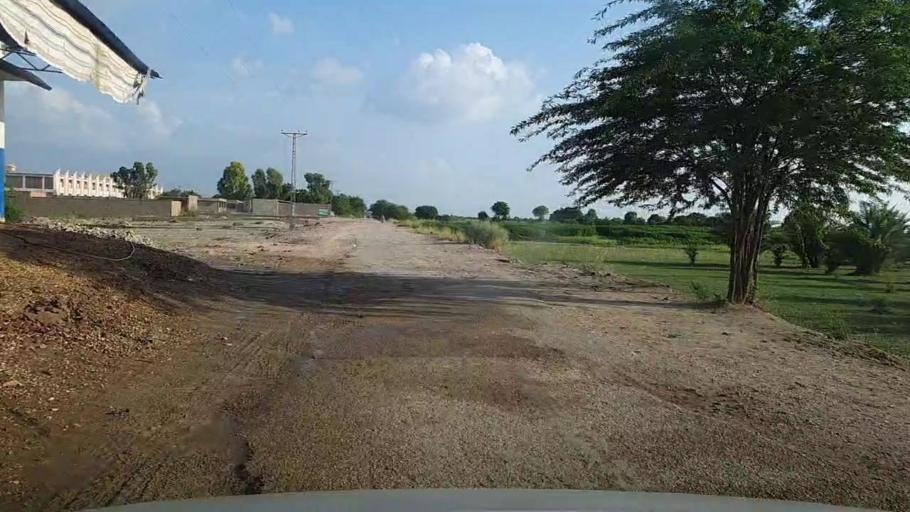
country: PK
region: Sindh
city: Hingorja
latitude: 27.0839
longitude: 68.4188
